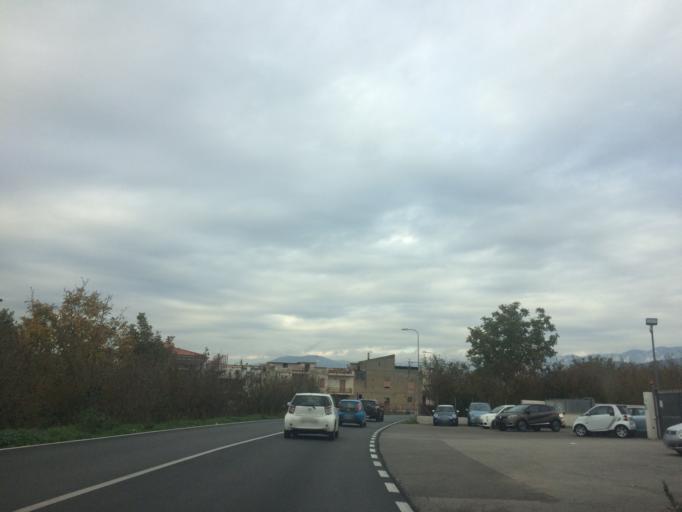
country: IT
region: Campania
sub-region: Provincia di Napoli
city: Piazzolla
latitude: 40.9010
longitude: 14.5253
